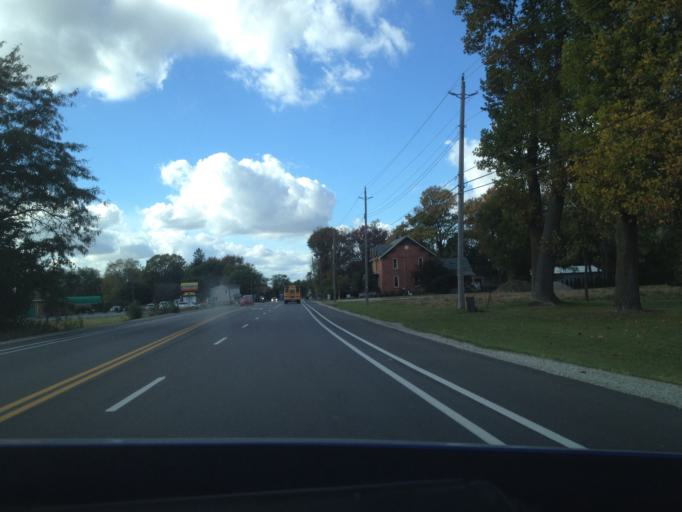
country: CA
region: Ontario
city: Amherstburg
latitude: 42.0362
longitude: -82.7129
